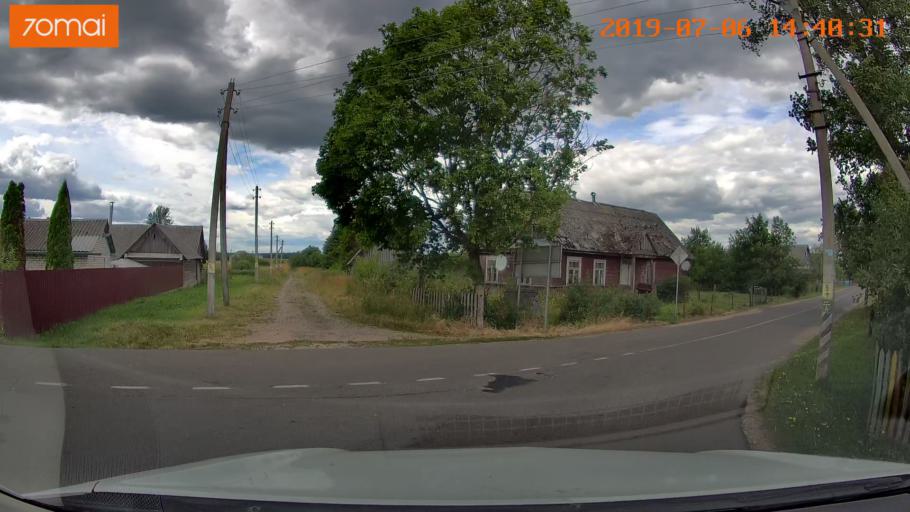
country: BY
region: Minsk
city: Ivyanyets
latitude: 53.9249
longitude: 26.6734
